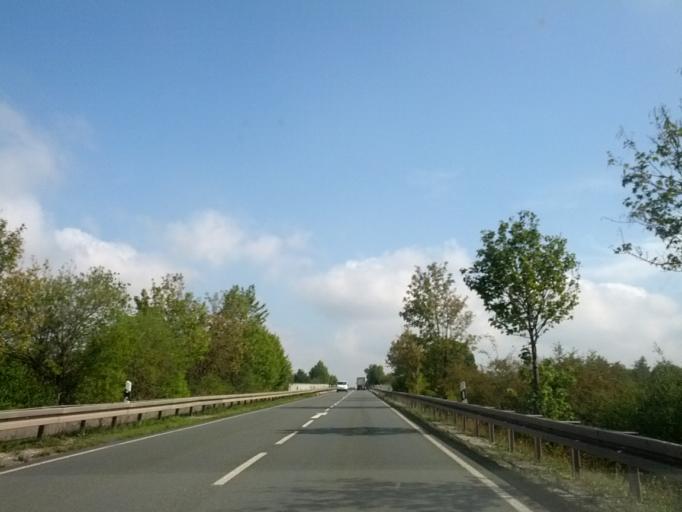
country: DE
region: Thuringia
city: Apfelstadt
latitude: 50.8951
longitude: 10.8951
